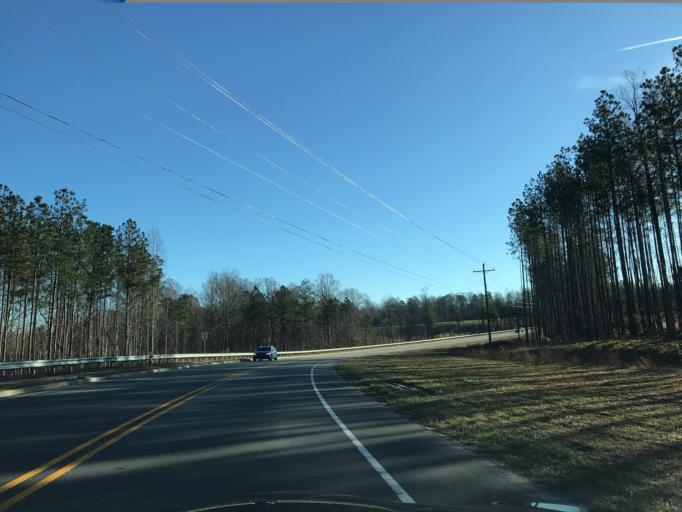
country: US
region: North Carolina
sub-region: Wake County
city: Morrisville
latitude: 35.9040
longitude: -78.7436
